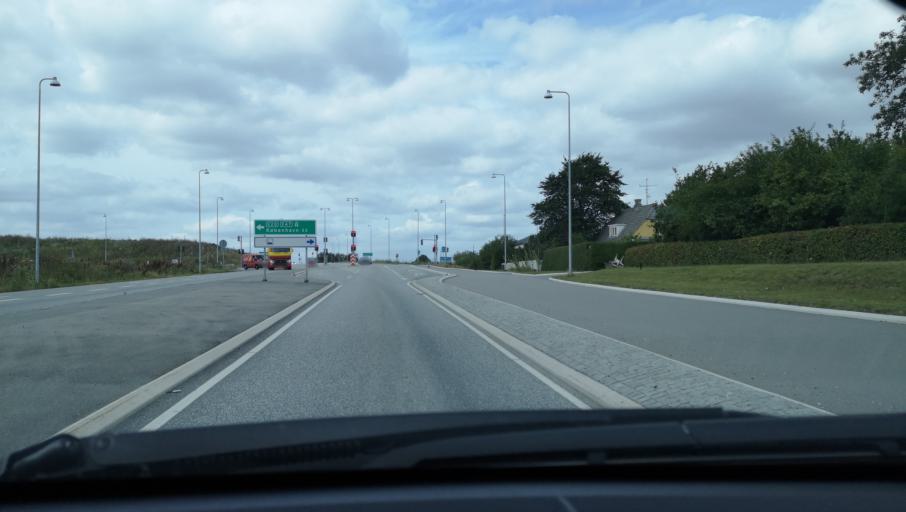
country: DK
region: Zealand
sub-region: Solrod Kommune
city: Solrod
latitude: 55.5042
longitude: 12.1805
